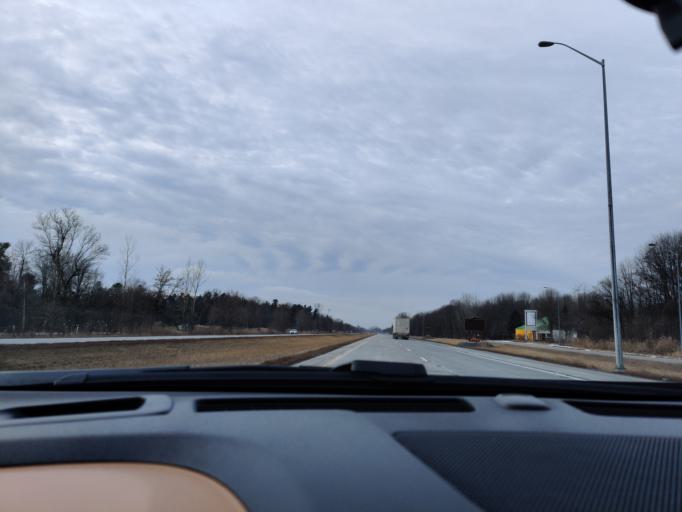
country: CA
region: Quebec
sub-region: Monteregie
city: Les Coteaux
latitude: 45.1560
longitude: -74.4612
